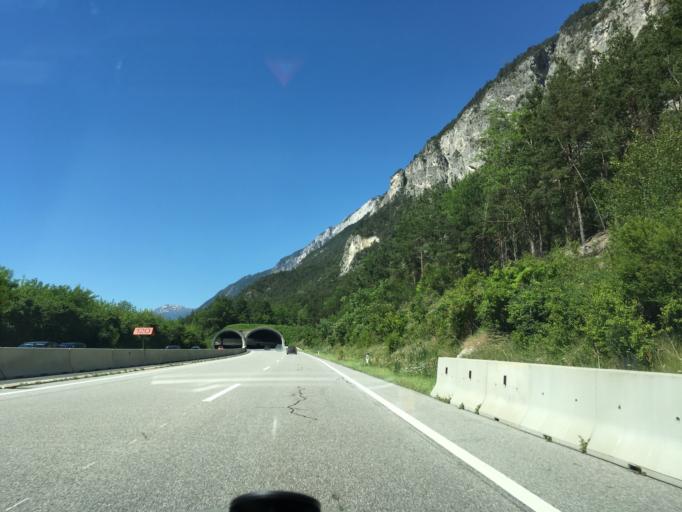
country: AT
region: Tyrol
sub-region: Politischer Bezirk Imst
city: Haiming
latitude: 47.2610
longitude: 10.8774
